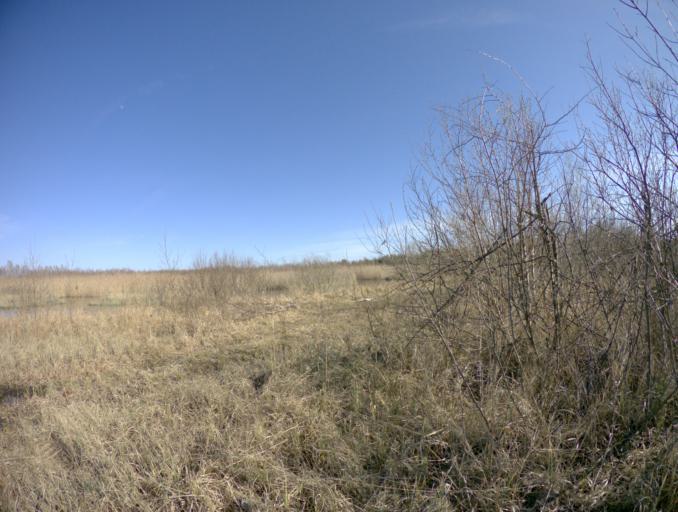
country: RU
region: Vladimir
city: Ivanishchi
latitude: 55.7166
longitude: 40.4310
